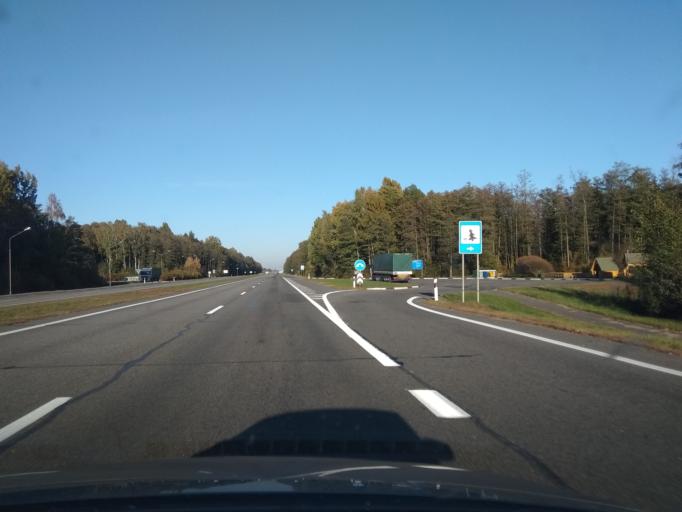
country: BY
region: Brest
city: Ivatsevichy
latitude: 52.6852
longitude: 25.3367
